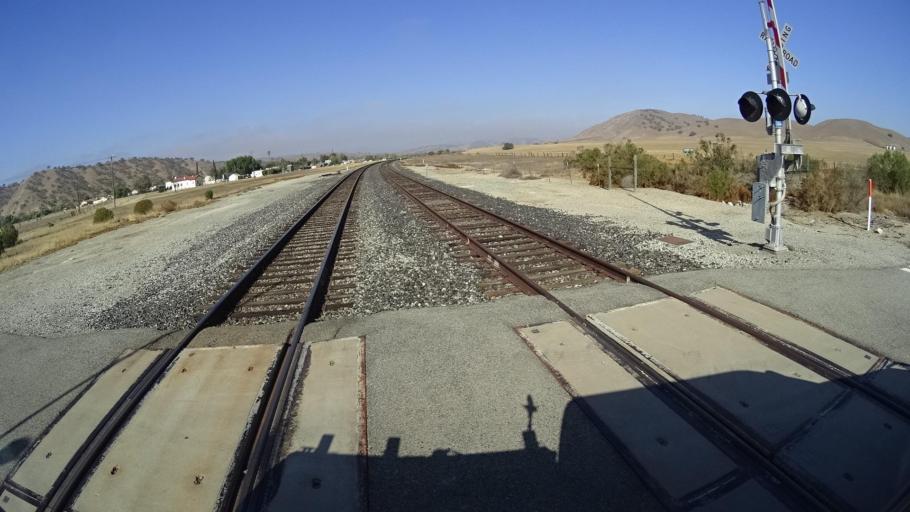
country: US
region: California
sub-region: San Luis Obispo County
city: San Miguel
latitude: 35.8639
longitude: -120.7957
